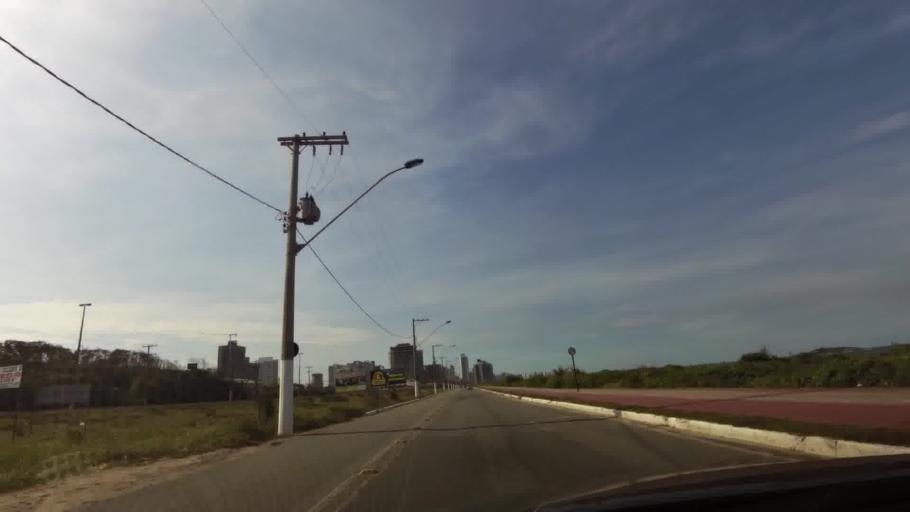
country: BR
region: Espirito Santo
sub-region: Vila Velha
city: Vila Velha
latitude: -20.3886
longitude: -40.3129
